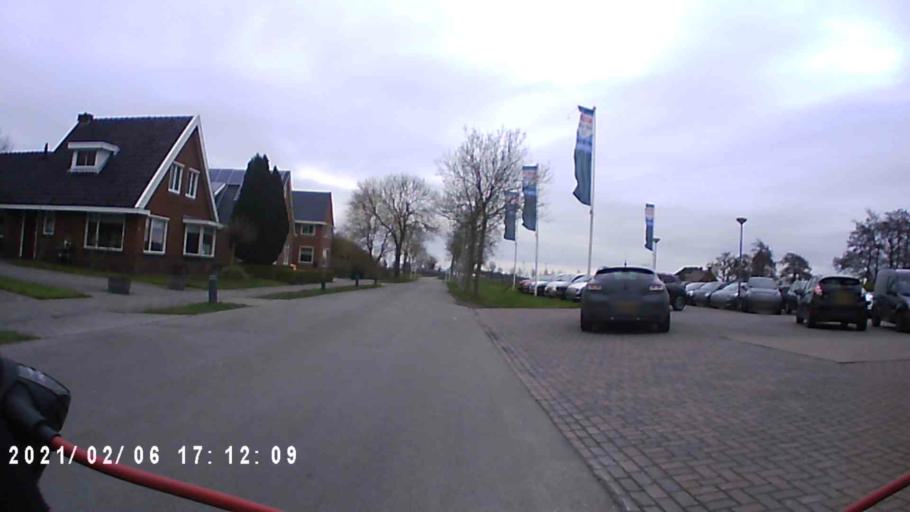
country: NL
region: Groningen
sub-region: Gemeente Appingedam
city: Appingedam
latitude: 53.4205
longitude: 6.7710
